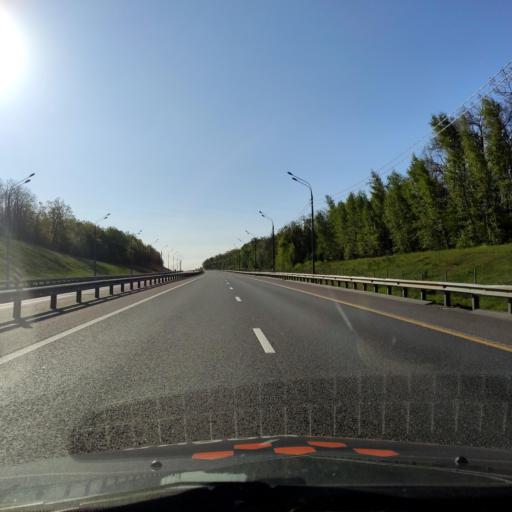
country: RU
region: Lipetsk
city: Khlevnoye
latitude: 52.2234
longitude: 39.1105
